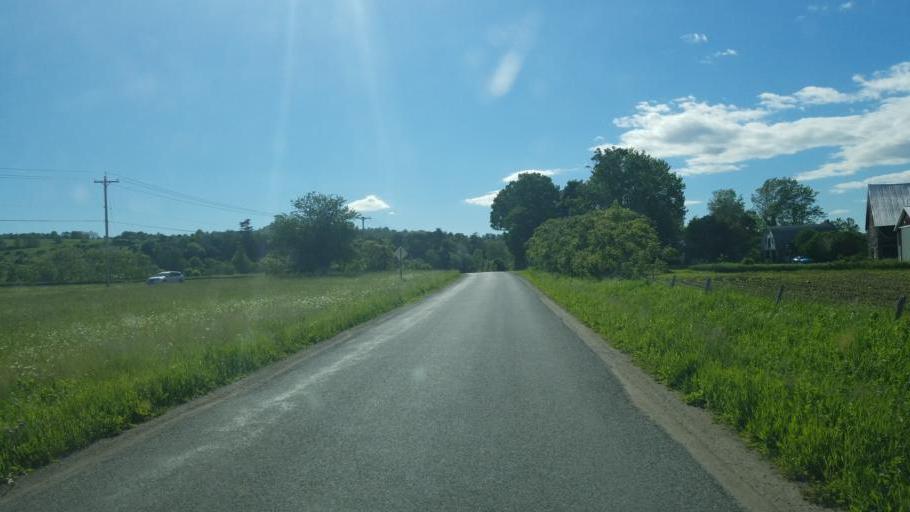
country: US
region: New York
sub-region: Herkimer County
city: Little Falls
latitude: 43.0037
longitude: -74.7757
